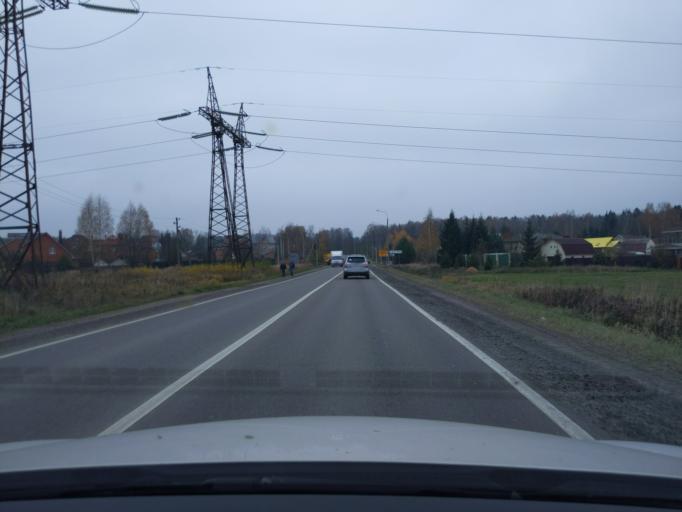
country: RU
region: Moskovskaya
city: Ashukino
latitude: 56.1571
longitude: 37.9598
